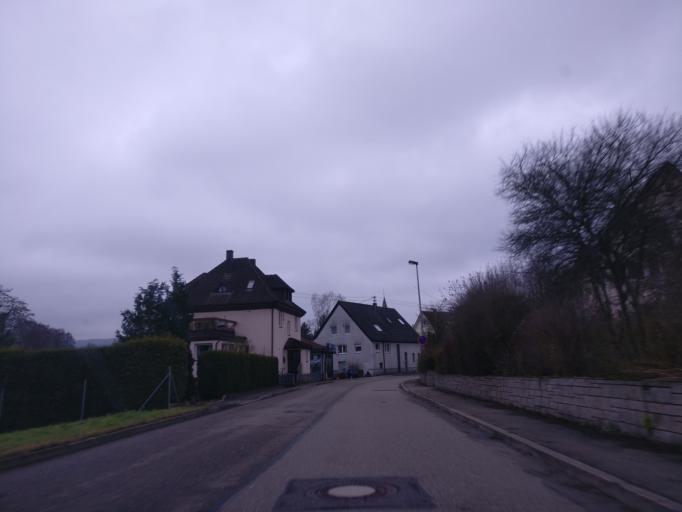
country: DE
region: Baden-Wuerttemberg
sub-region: Regierungsbezirk Stuttgart
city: Allmersbach im Tal
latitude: 48.8607
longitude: 9.4733
